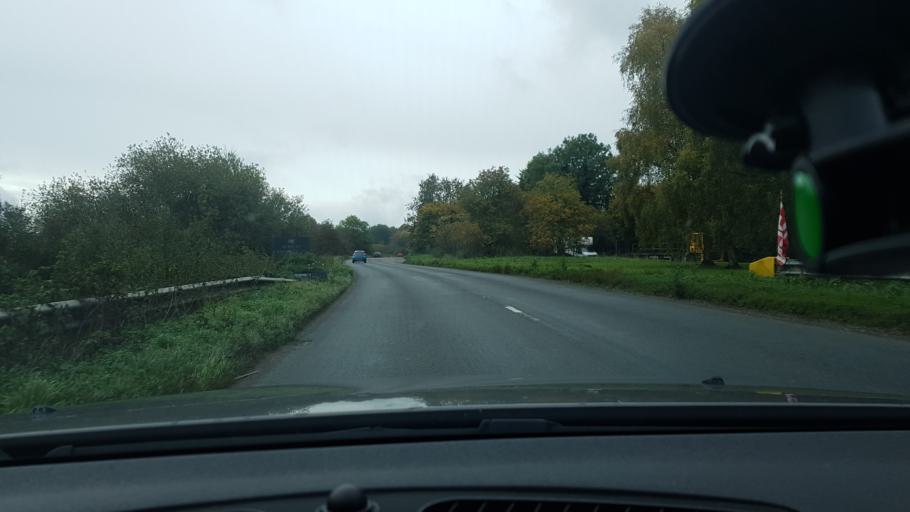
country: GB
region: England
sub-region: Wiltshire
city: Marlborough
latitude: 51.4374
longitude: -1.7319
